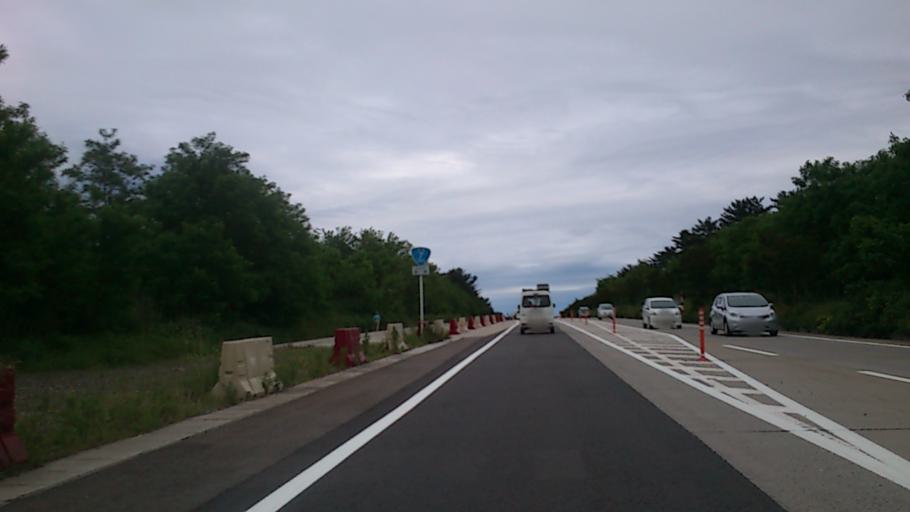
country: JP
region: Akita
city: Akita Shi
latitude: 39.7087
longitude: 140.0734
